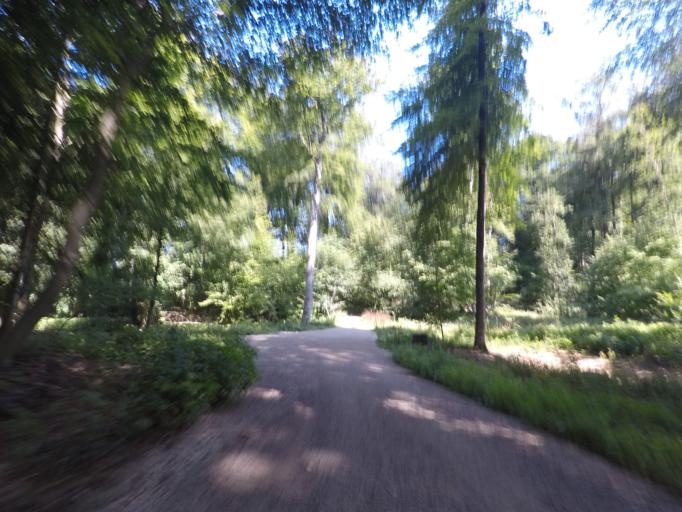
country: LU
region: Luxembourg
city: Bridel
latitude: 49.6519
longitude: 6.0734
